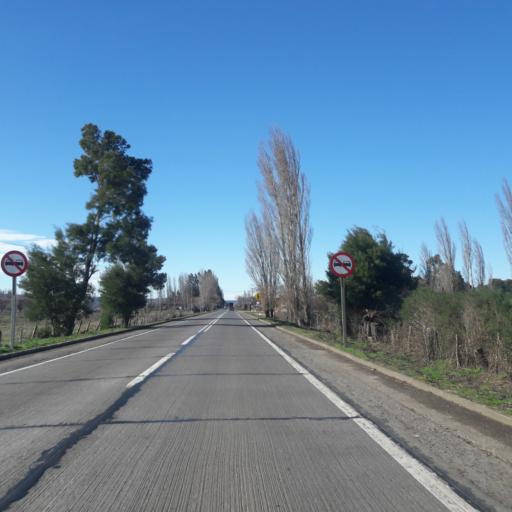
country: CL
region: Araucania
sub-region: Provincia de Malleco
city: Angol
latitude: -37.7686
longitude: -72.5557
